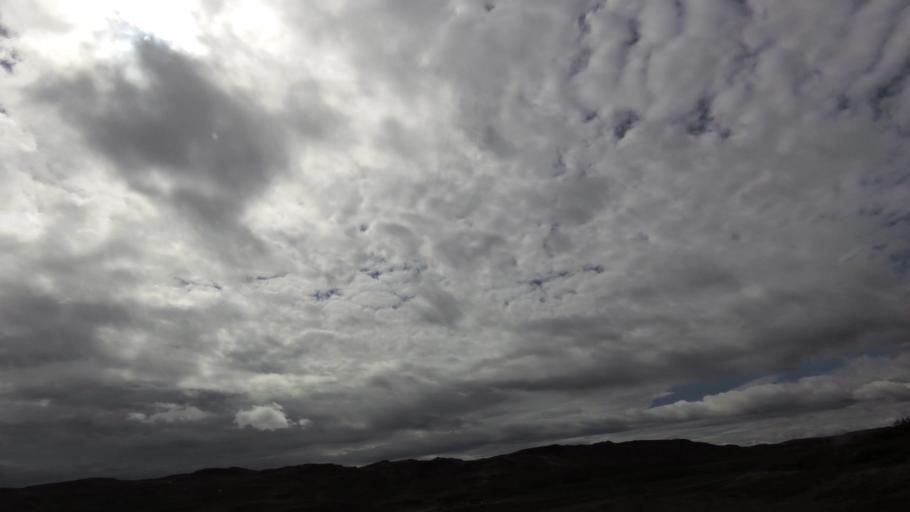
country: IS
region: West
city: Stykkisholmur
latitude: 65.5345
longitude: -22.0857
